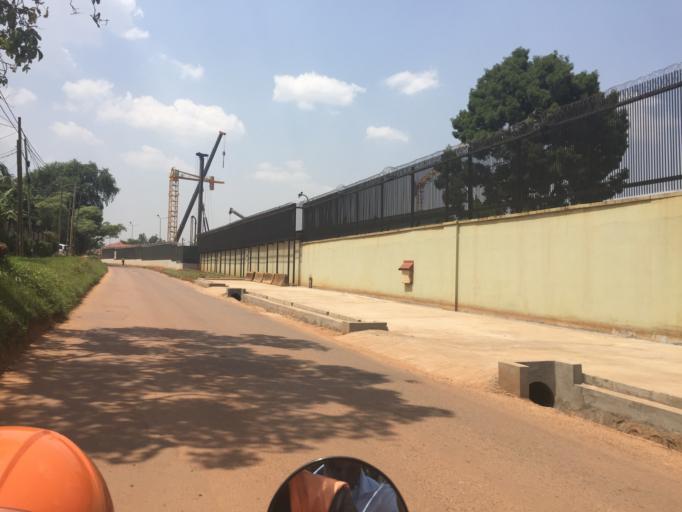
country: UG
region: Central Region
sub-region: Kampala District
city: Kampala
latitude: 0.2996
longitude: 32.5918
